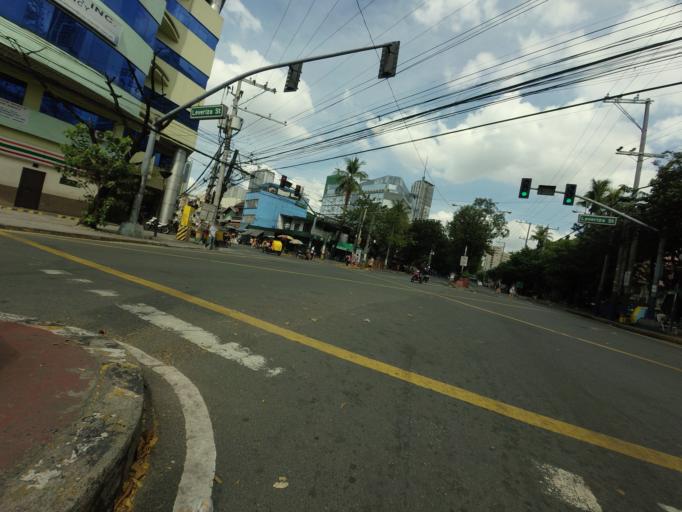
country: PH
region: Metro Manila
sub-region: City of Manila
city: Port Area
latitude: 14.5677
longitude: 120.9895
